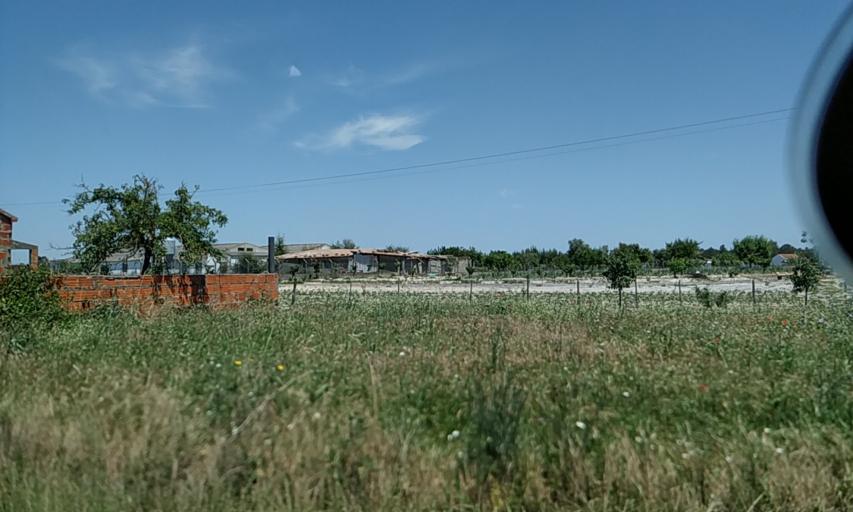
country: PT
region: Setubal
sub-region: Palmela
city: Pinhal Novo
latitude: 38.6406
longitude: -8.7427
